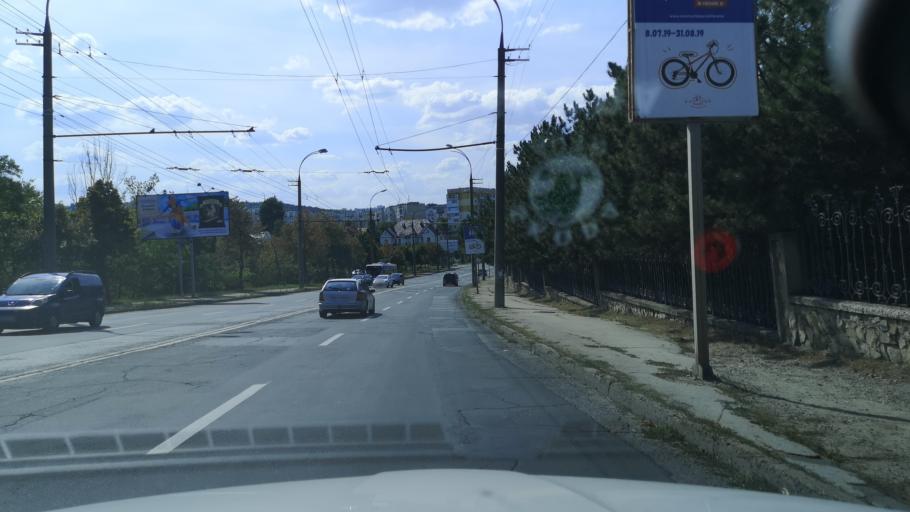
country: MD
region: Chisinau
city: Chisinau
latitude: 47.0235
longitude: 28.8138
